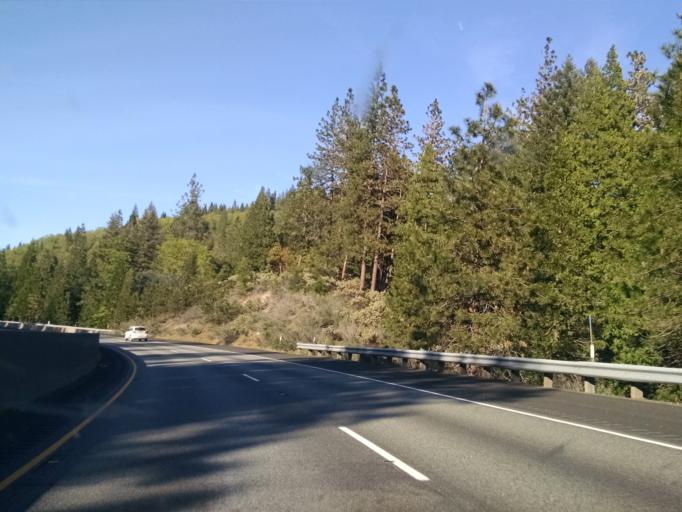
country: US
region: California
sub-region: Siskiyou County
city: Dunsmuir
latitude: 41.0835
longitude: -122.3526
